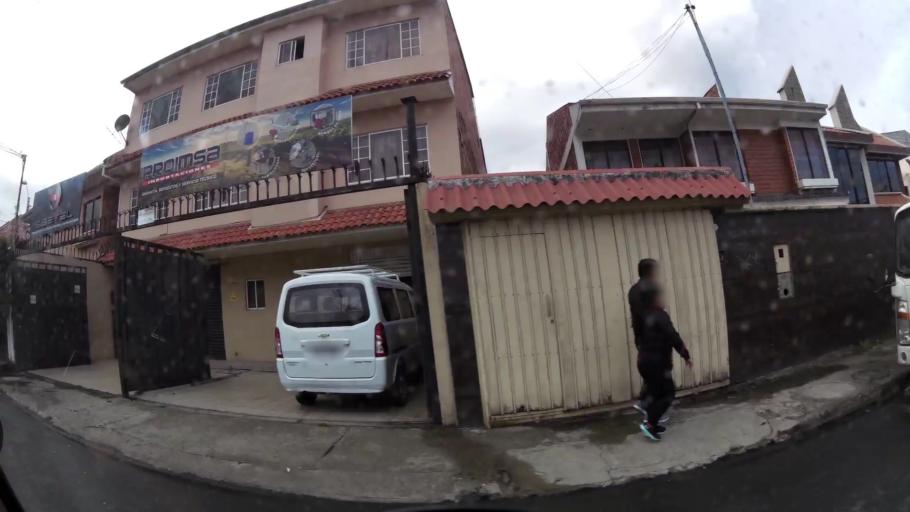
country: EC
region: Azuay
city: Cuenca
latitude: -2.8967
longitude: -79.0203
